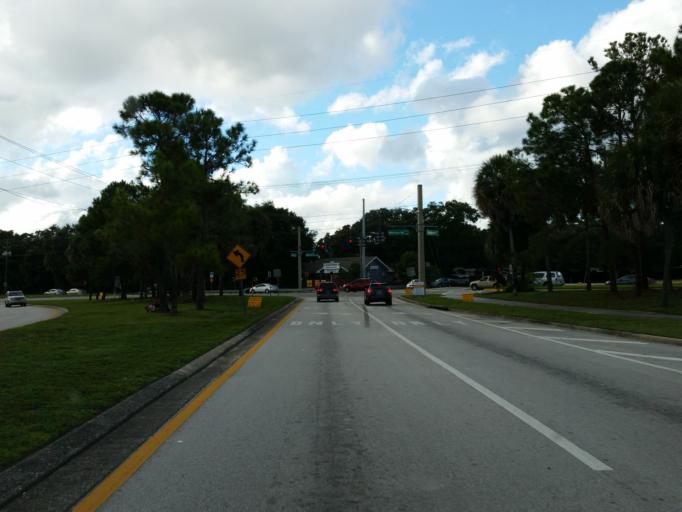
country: US
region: Florida
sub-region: Hillsborough County
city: Town 'n' Country
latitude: 27.9812
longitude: -82.5561
